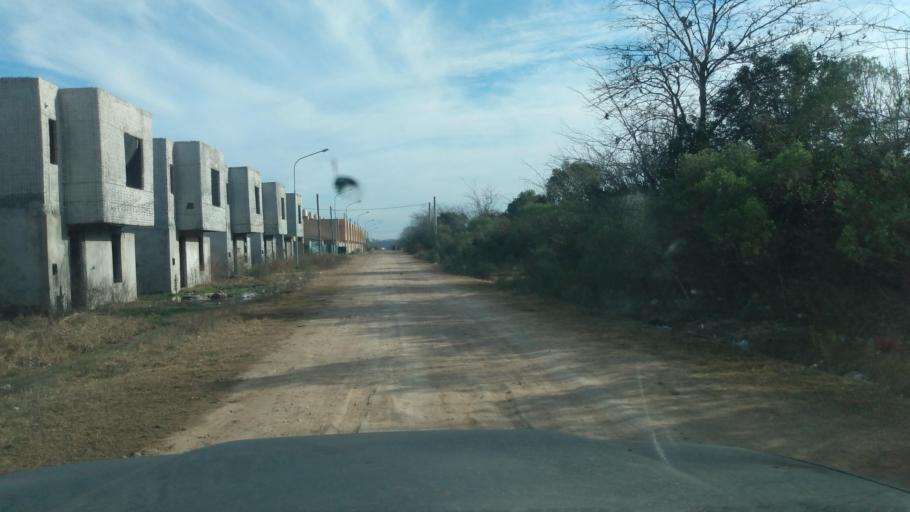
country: AR
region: Buenos Aires
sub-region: Partido de Lujan
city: Lujan
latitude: -34.5382
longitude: -59.1130
